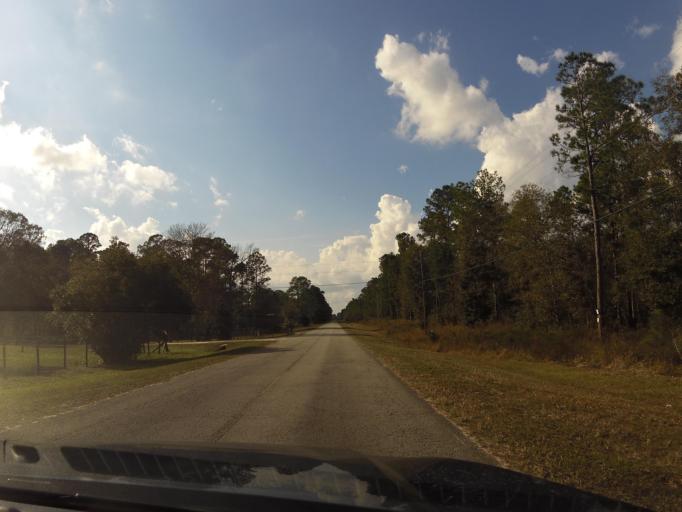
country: US
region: Florida
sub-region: Duval County
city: Baldwin
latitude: 30.1578
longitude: -81.9850
